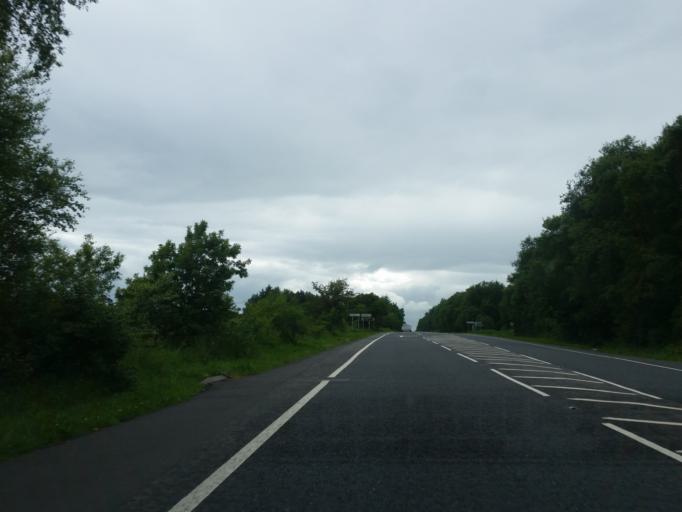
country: GB
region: Northern Ireland
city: Fivemiletown
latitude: 54.3387
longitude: -7.3628
